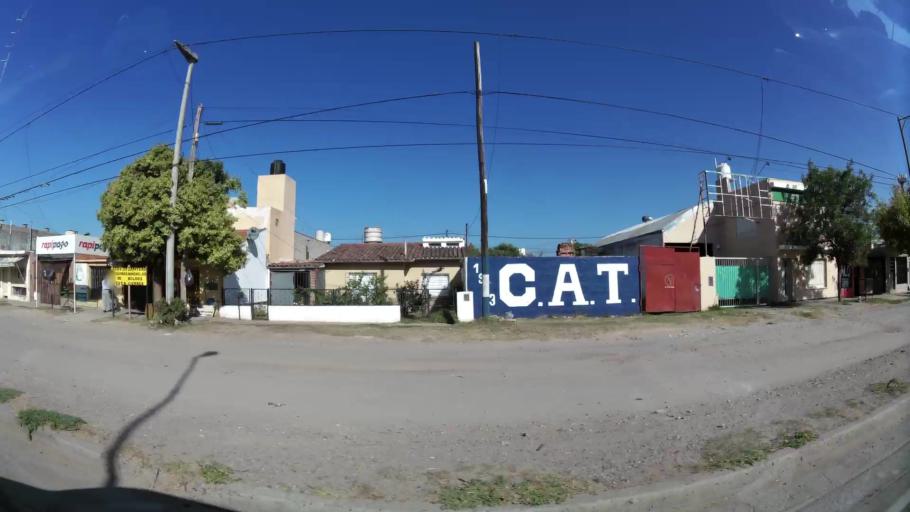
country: AR
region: Cordoba
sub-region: Departamento de Capital
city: Cordoba
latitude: -31.4676
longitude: -64.2249
